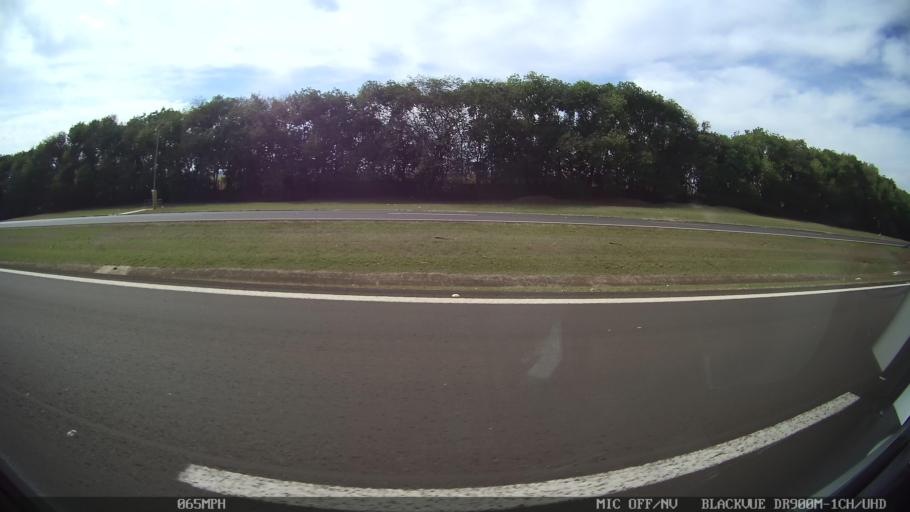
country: BR
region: Sao Paulo
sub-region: Matao
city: Matao
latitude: -21.6325
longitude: -48.4024
